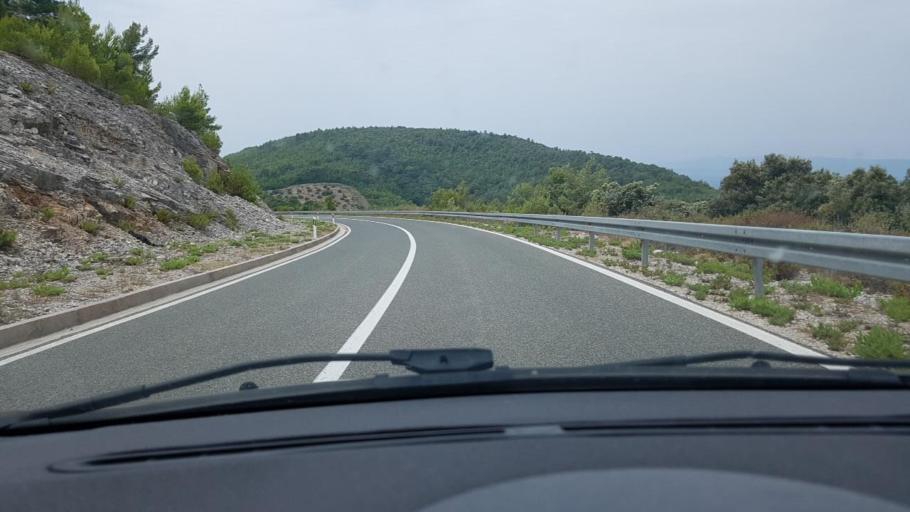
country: HR
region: Dubrovacko-Neretvanska
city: Smokvica
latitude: 42.9568
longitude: 16.9406
